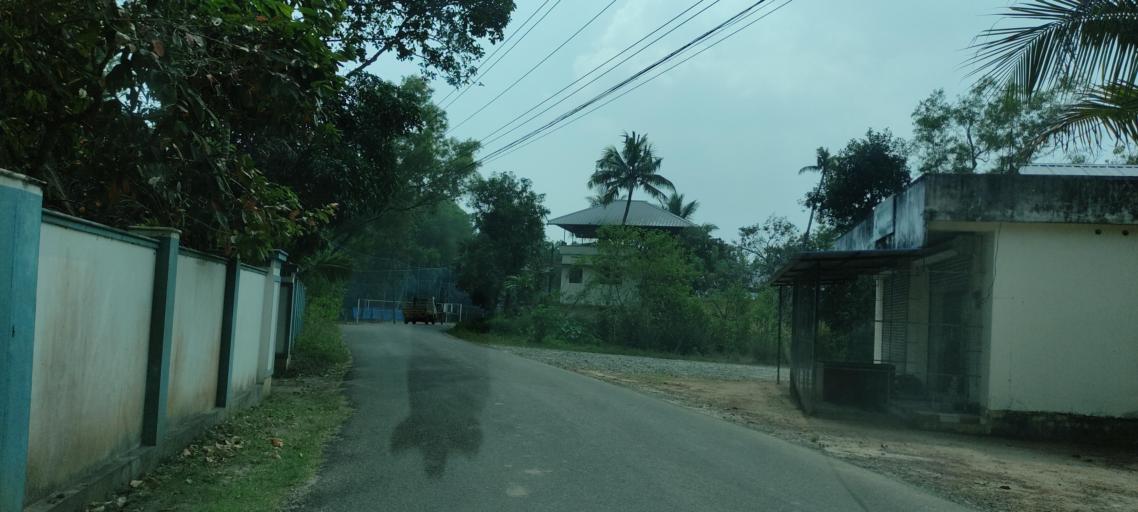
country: IN
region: Kerala
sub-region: Alappuzha
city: Shertallai
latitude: 9.6188
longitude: 76.3481
